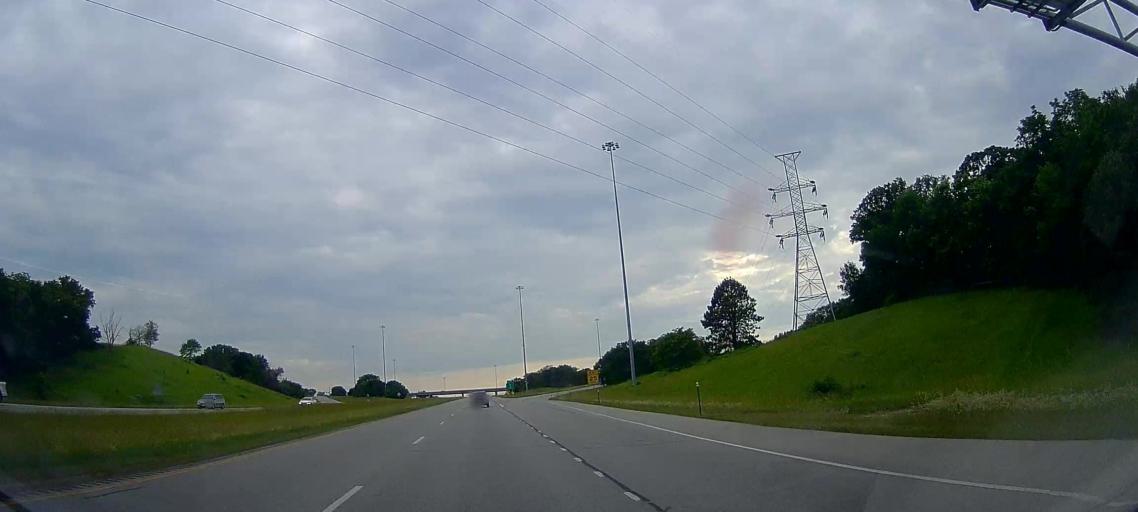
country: US
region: Iowa
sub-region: Pottawattamie County
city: Carter Lake
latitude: 41.3432
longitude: -96.0186
